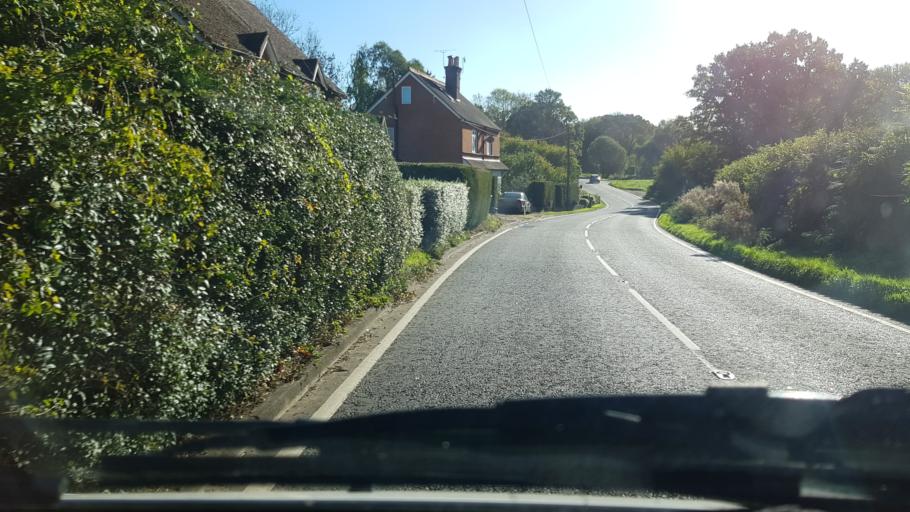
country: GB
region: England
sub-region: Surrey
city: Chilworth
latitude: 51.1748
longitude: -0.5164
